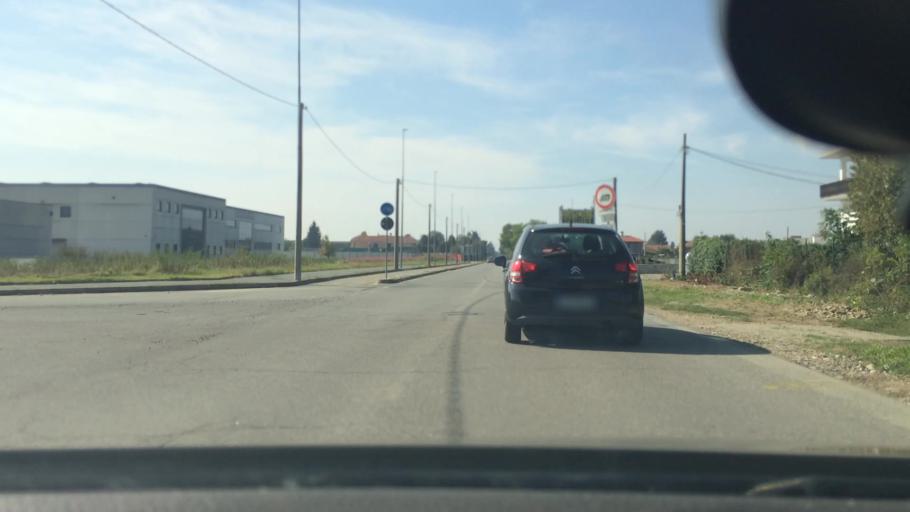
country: IT
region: Lombardy
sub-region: Citta metropolitana di Milano
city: Cerro Maggiore
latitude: 45.6020
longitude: 8.9663
